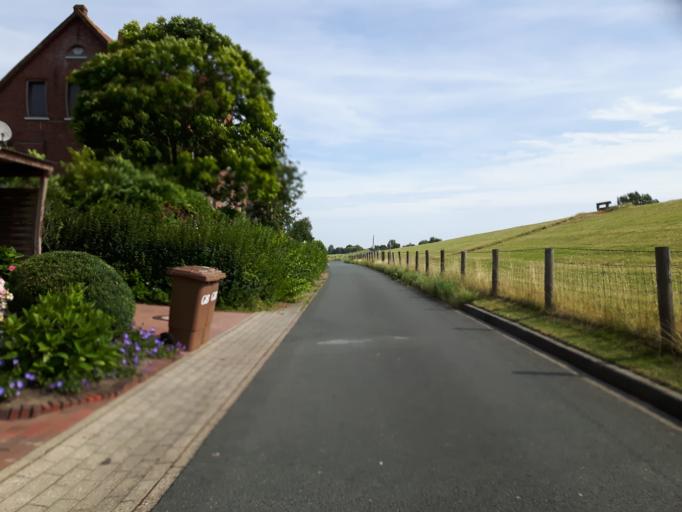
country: DE
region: Lower Saxony
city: Elsfleth
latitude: 53.2540
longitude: 8.4737
